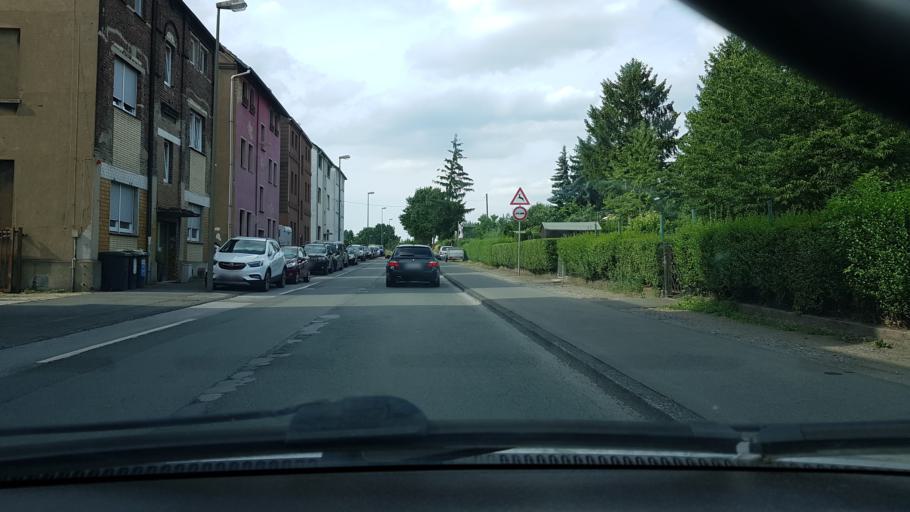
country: DE
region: North Rhine-Westphalia
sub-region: Regierungsbezirk Arnsberg
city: Dortmund
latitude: 51.5589
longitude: 7.4434
